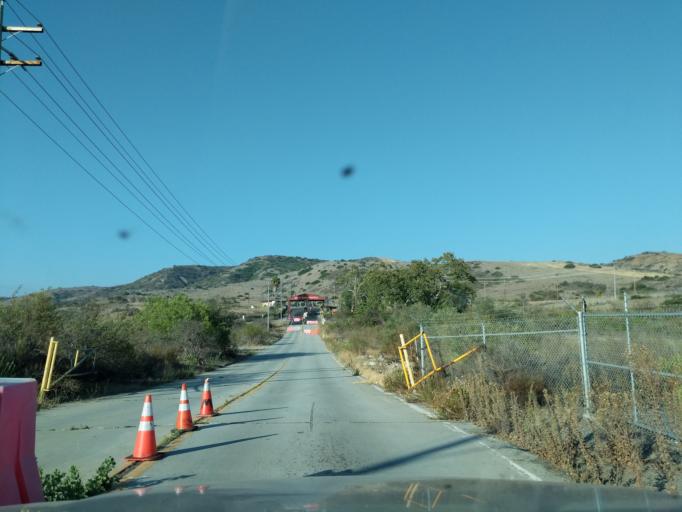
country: US
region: California
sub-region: Orange County
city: San Clemente
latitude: 33.4259
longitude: -117.5707
